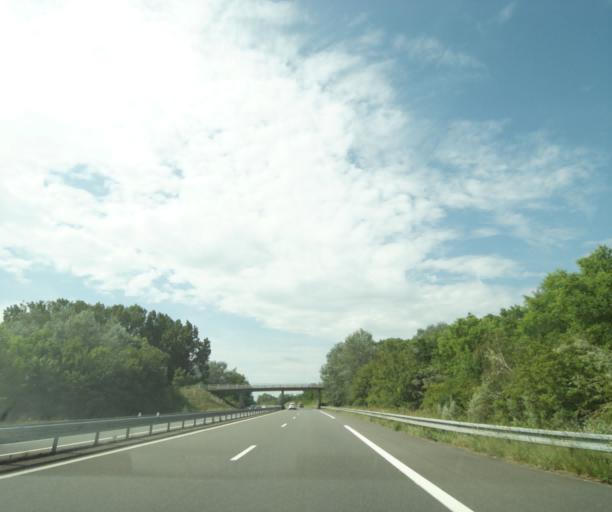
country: FR
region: Pays de la Loire
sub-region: Departement de Maine-et-Loire
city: Saint-Philbert-du-Peuple
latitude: 47.3792
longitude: -0.0861
